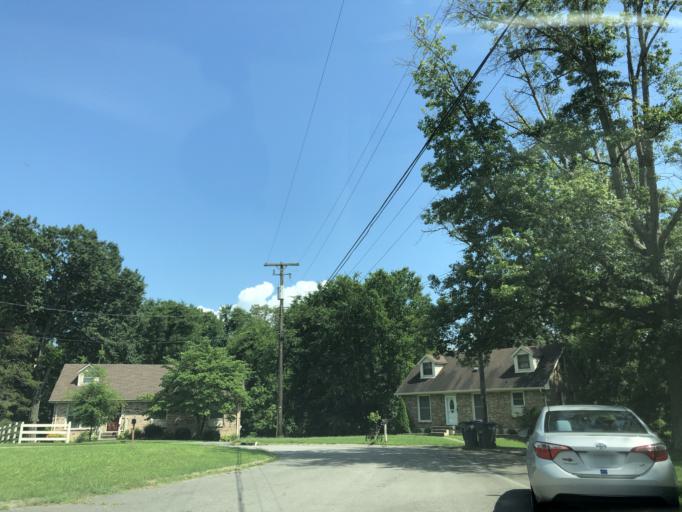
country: US
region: Tennessee
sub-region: Wilson County
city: Green Hill
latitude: 36.2216
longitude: -86.5857
